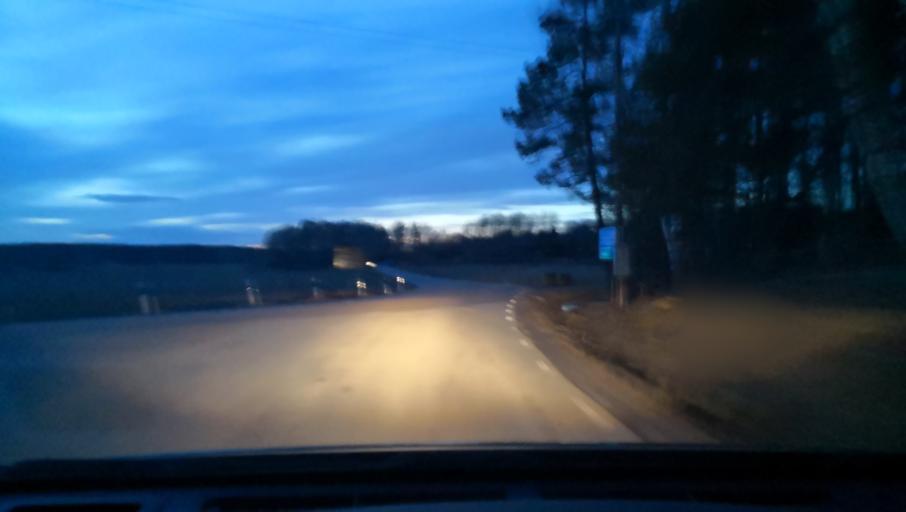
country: SE
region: Uppsala
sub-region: Enkopings Kommun
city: Grillby
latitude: 59.6082
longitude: 17.2766
